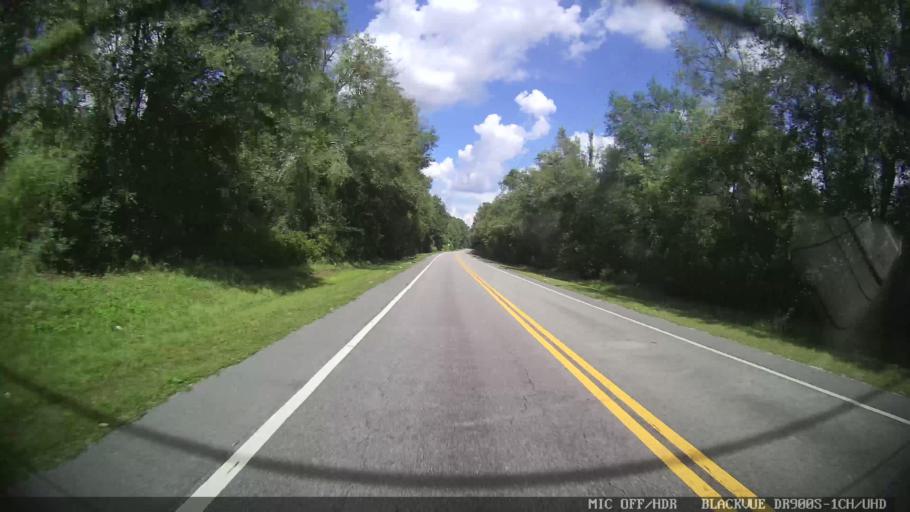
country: US
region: Florida
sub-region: Hamilton County
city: Jasper
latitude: 30.5559
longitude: -83.0804
